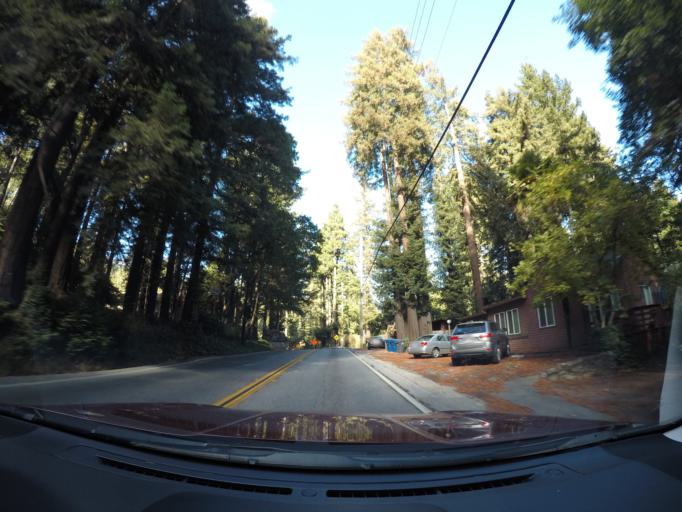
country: US
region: California
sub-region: Santa Cruz County
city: Brookdale
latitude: 37.1072
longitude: -122.1074
